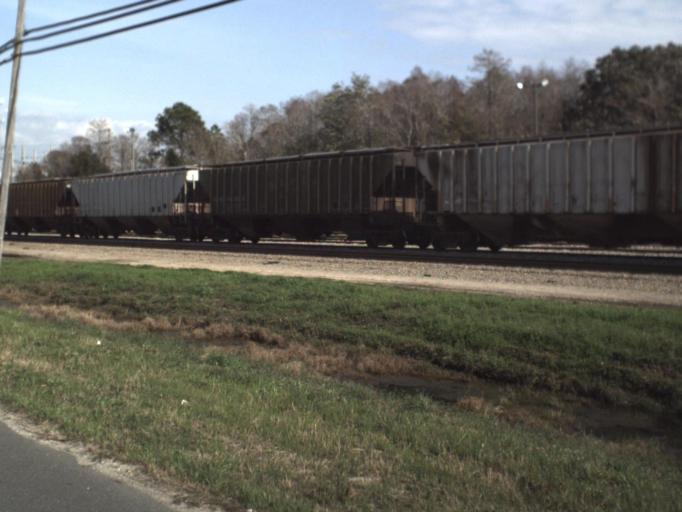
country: US
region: Florida
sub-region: Bay County
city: Hiland Park
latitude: 30.1933
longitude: -85.6354
